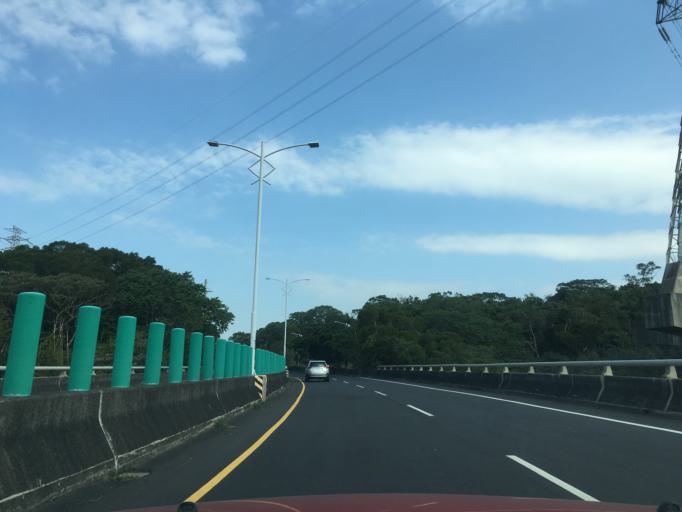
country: TW
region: Taiwan
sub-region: Hsinchu
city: Hsinchu
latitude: 24.7637
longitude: 121.0084
